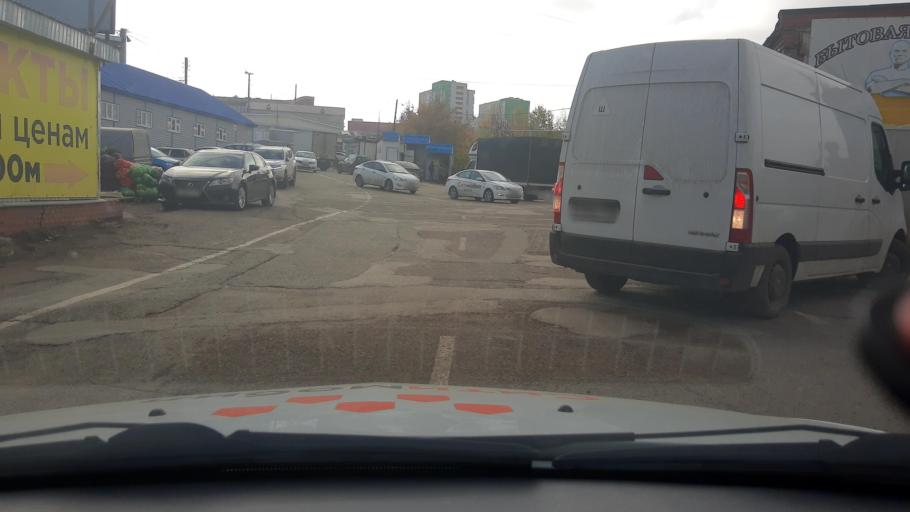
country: RU
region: Bashkortostan
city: Ufa
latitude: 54.7149
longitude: 55.9865
